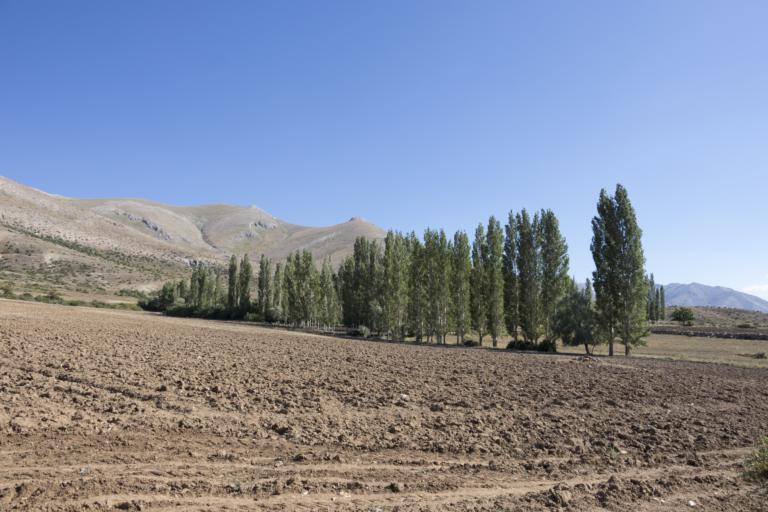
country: TR
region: Kayseri
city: Toklar
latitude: 38.3959
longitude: 36.0906
